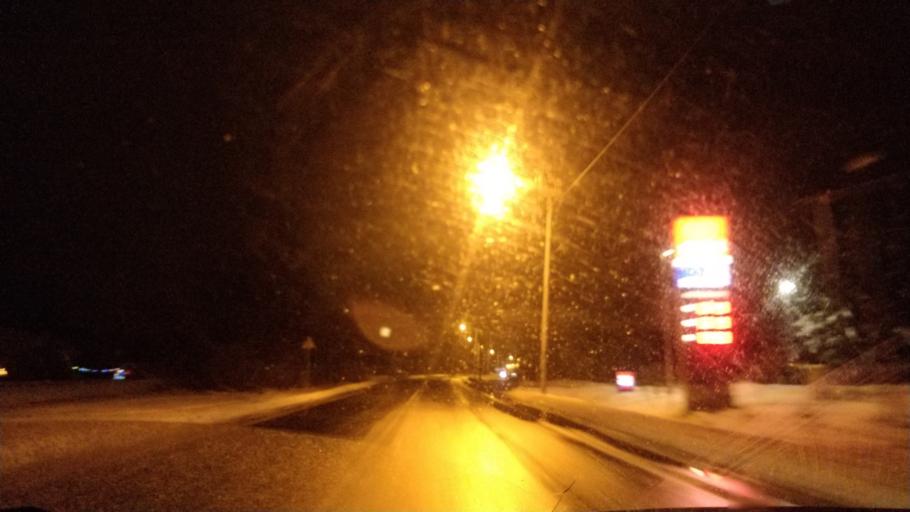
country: FI
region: Lapland
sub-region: Kemi-Tornio
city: Tervola
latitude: 66.1448
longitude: 24.9612
